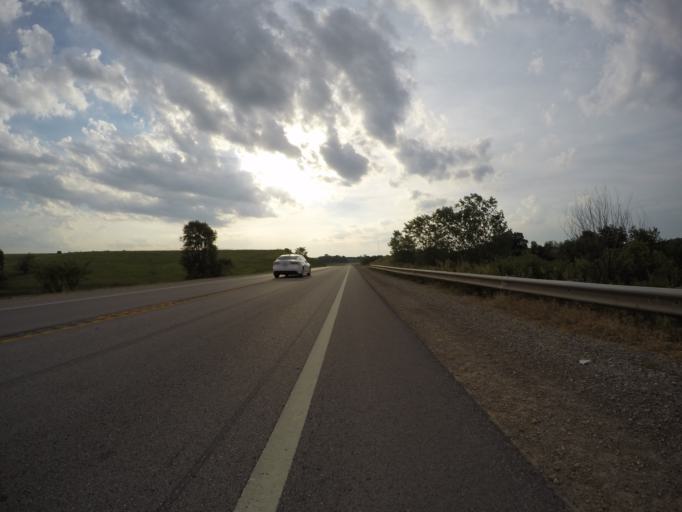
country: US
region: Kansas
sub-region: Doniphan County
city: Troy
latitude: 39.7931
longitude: -95.0613
